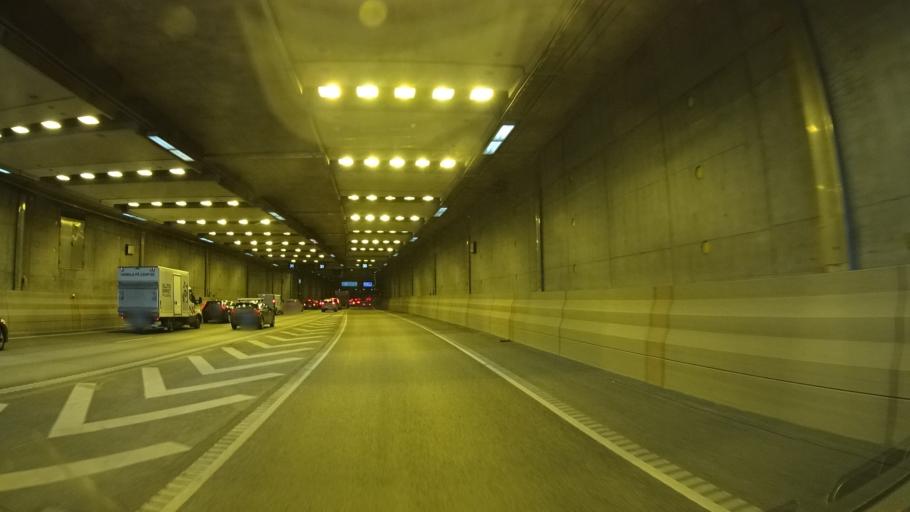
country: SE
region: Stockholm
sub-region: Stockholms Kommun
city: Arsta
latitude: 59.2953
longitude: 18.0399
